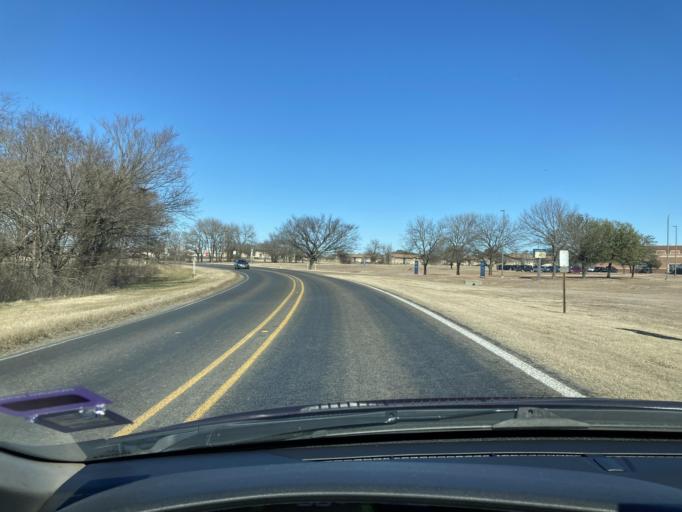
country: US
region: Texas
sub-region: Navarro County
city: Corsicana
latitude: 32.0675
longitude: -96.5017
